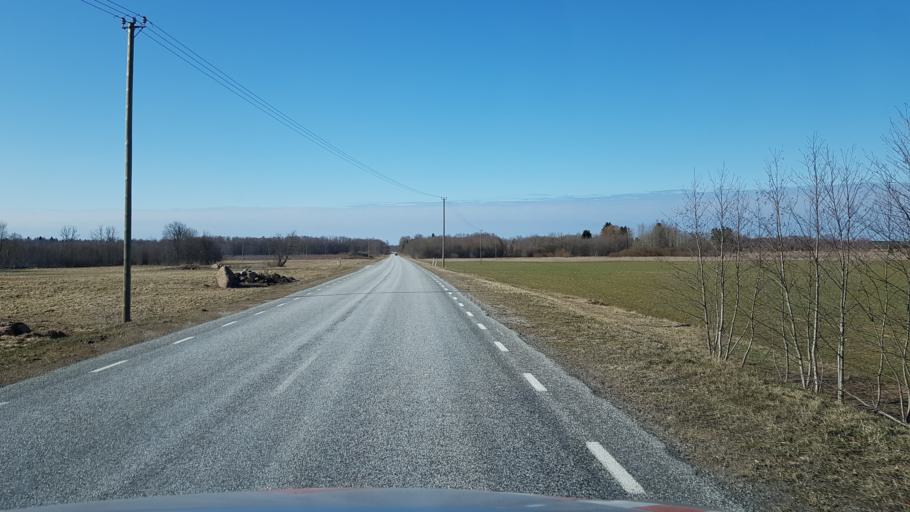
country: EE
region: Laeaene-Virumaa
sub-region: Haljala vald
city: Haljala
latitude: 59.4845
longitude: 26.1522
